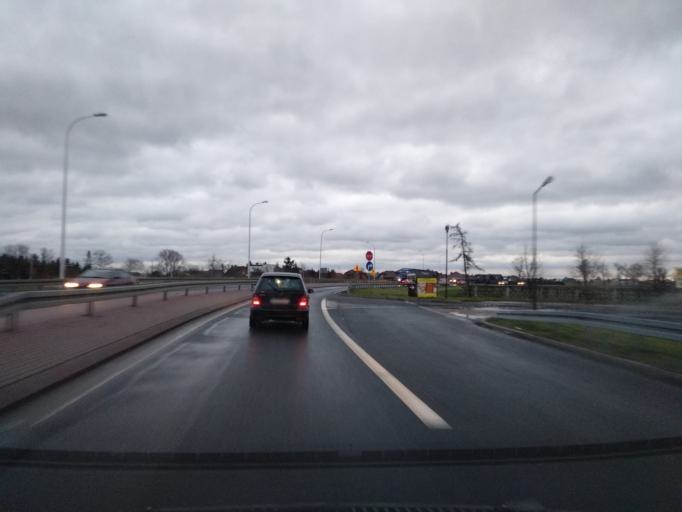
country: PL
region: Greater Poland Voivodeship
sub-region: Powiat koninski
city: Rychwal
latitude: 52.0671
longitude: 18.1628
